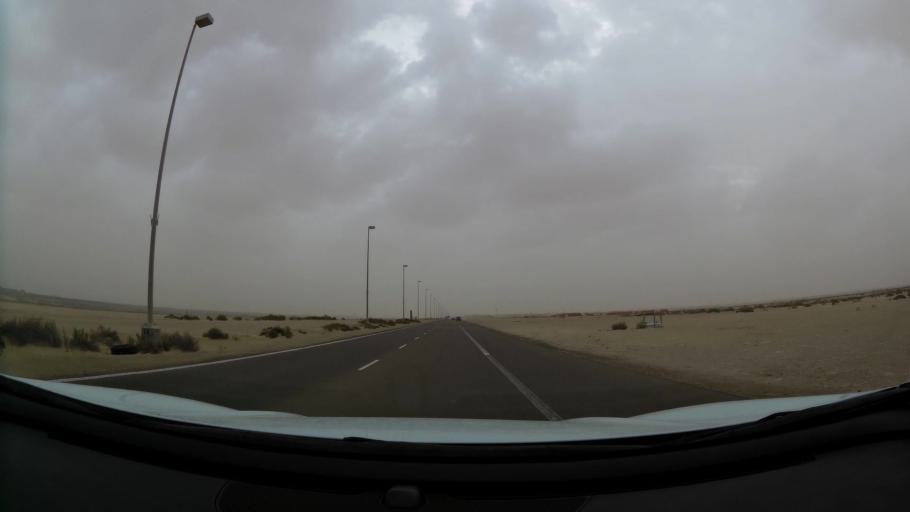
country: AE
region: Abu Dhabi
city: Abu Dhabi
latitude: 24.4611
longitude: 54.6972
